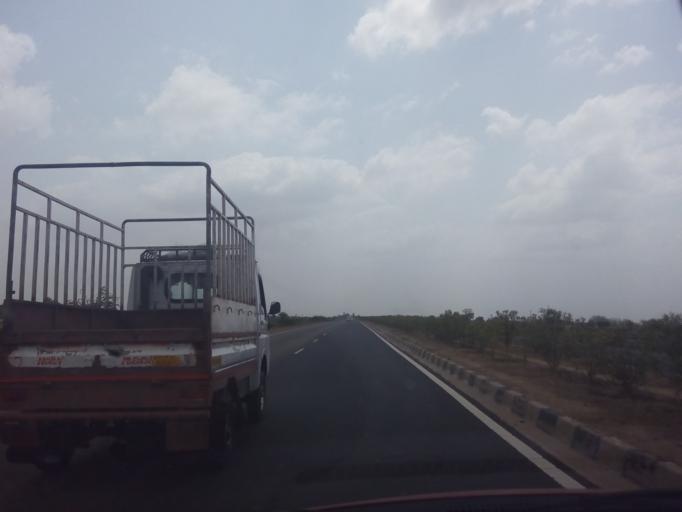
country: IN
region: Gujarat
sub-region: Surendranagar
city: Dhrangadhra
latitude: 23.0166
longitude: 71.5719
